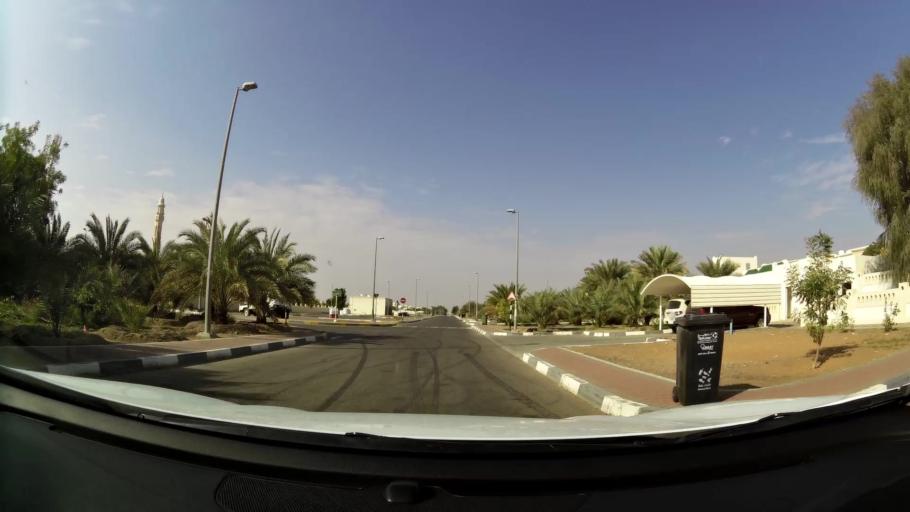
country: AE
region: Abu Dhabi
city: Al Ain
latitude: 24.0784
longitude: 55.8685
